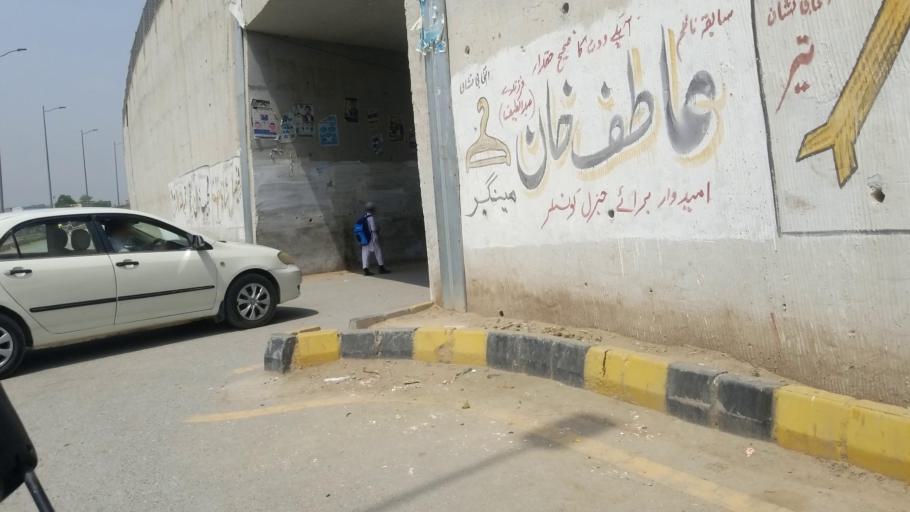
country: PK
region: Khyber Pakhtunkhwa
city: Peshawar
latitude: 34.0297
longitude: 71.5471
